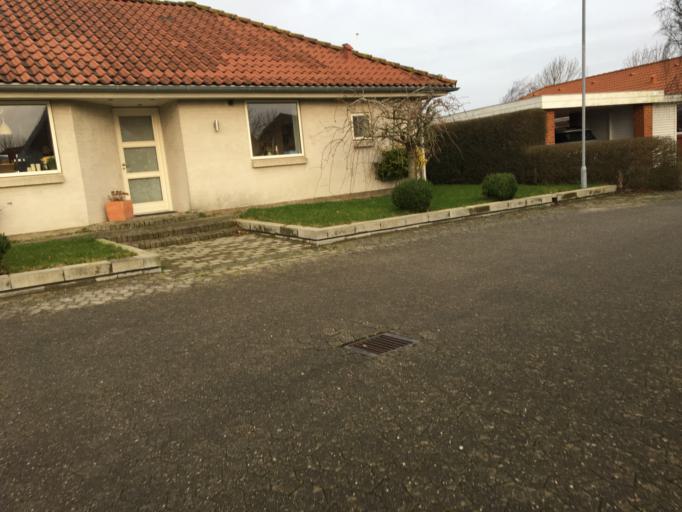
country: DK
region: Central Jutland
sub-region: Ringkobing-Skjern Kommune
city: Ringkobing
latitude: 56.0994
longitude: 8.2628
